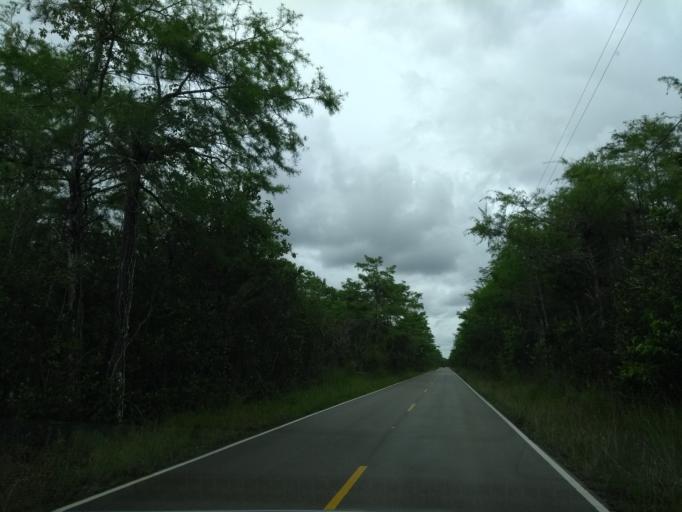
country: US
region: Florida
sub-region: Miami-Dade County
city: The Hammocks
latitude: 25.7613
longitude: -80.9113
